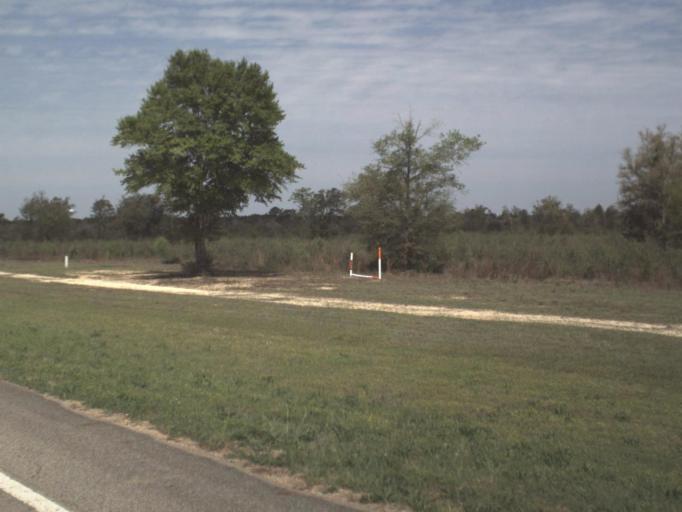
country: US
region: Florida
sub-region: Okaloosa County
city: Crestview
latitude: 30.7440
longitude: -86.4104
